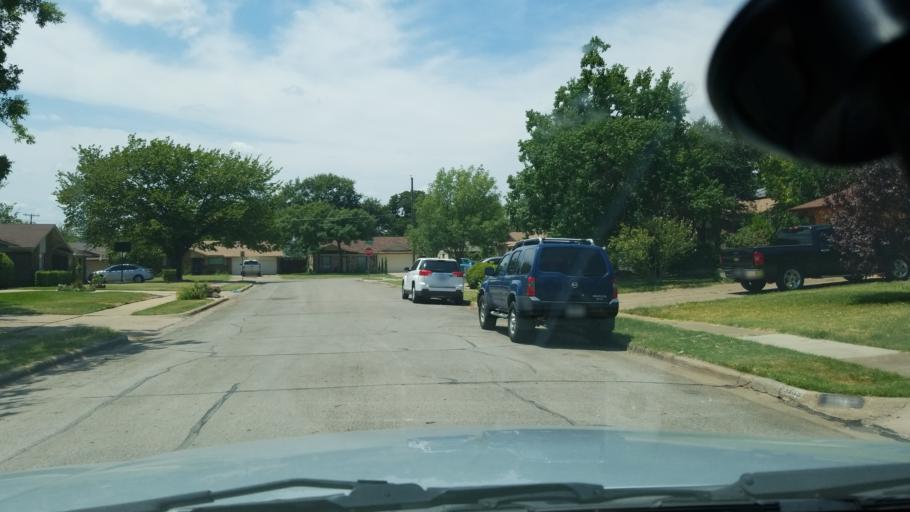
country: US
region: Texas
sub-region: Dallas County
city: Irving
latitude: 32.8256
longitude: -96.9894
